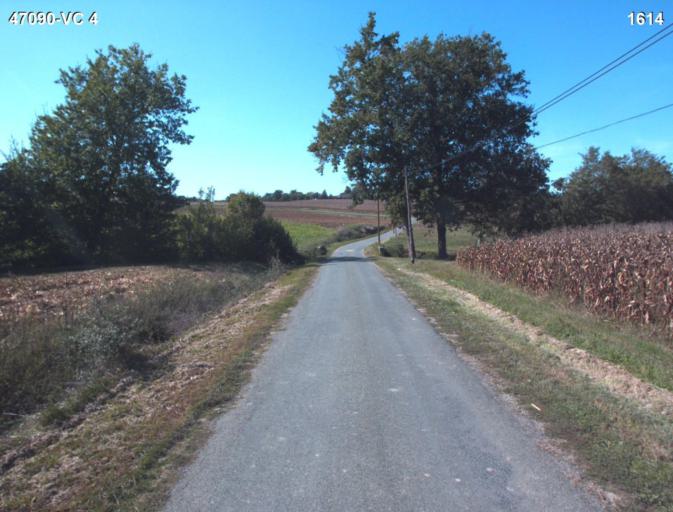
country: FR
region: Aquitaine
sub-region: Departement du Lot-et-Garonne
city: Vianne
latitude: 44.1780
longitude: 0.3612
